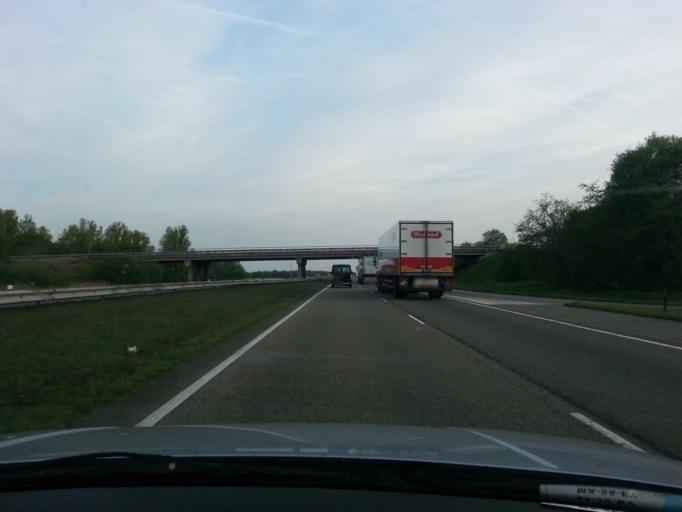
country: NL
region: Friesland
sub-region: Gemeente Skarsterlan
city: Sint Nicolaasga
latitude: 52.9179
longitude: 5.7753
